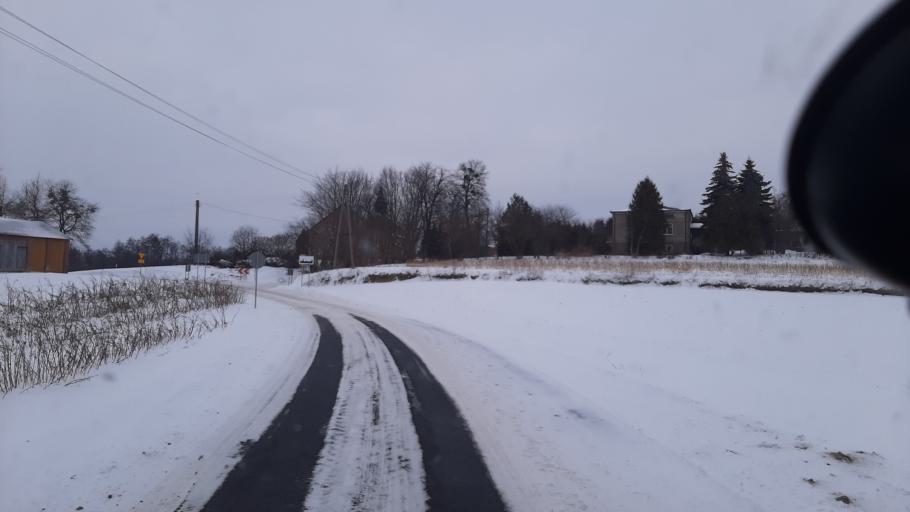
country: PL
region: Lublin Voivodeship
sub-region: Powiat lubelski
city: Garbow
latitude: 51.3415
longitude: 22.2931
